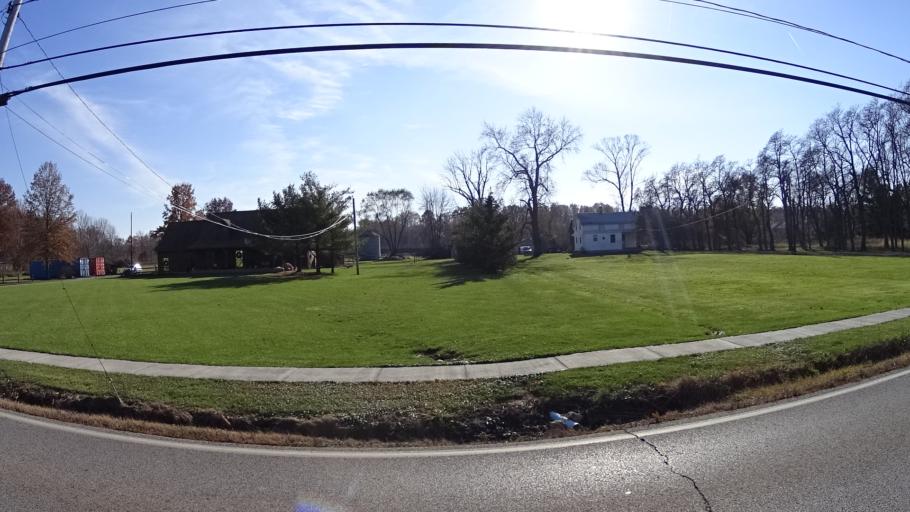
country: US
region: Ohio
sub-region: Lorain County
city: Avon
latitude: 41.4671
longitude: -82.0386
